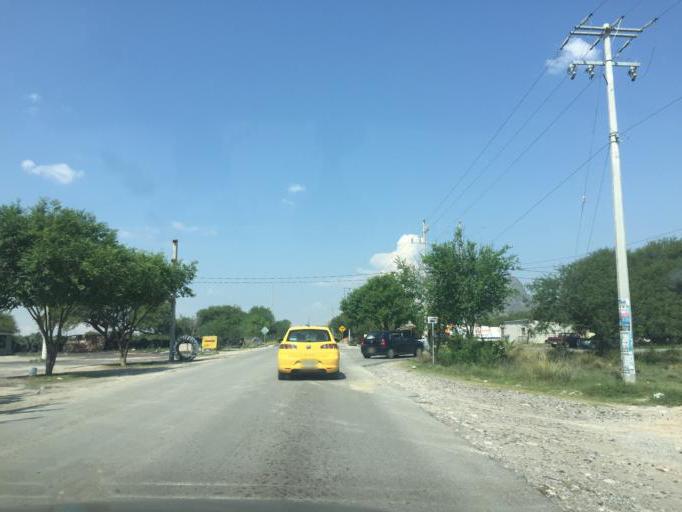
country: MX
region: Hidalgo
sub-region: Cardonal
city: Pozuelos
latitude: 20.6088
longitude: -99.0977
